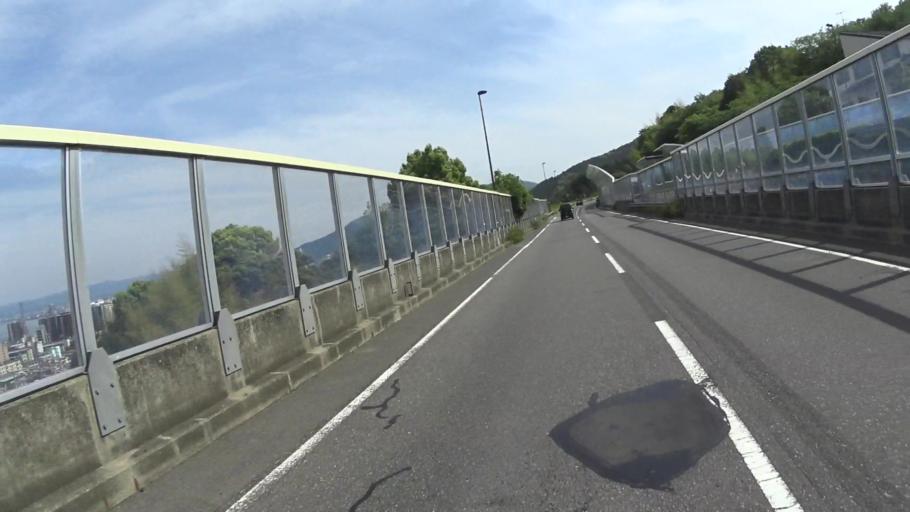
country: JP
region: Shiga Prefecture
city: Otsu-shi
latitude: 35.0283
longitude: 135.8503
